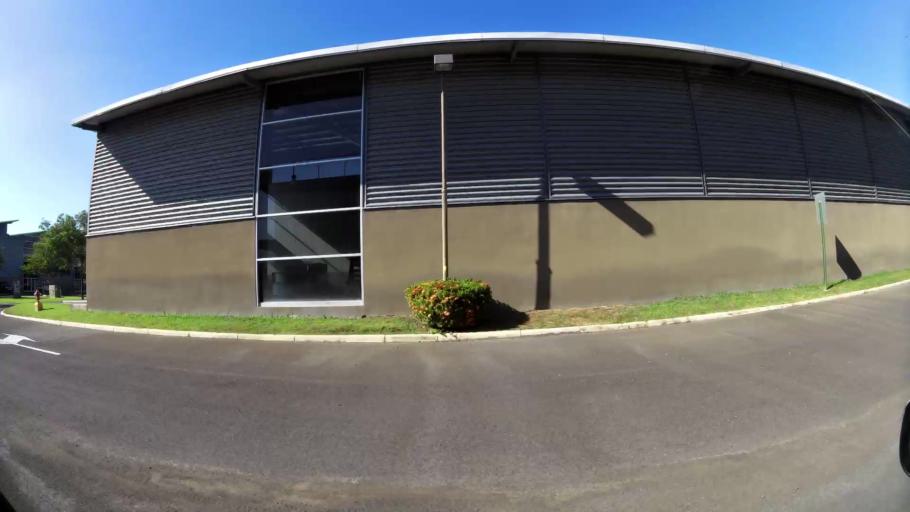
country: CR
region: Guanacaste
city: Liberia
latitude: 10.5893
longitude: -85.5338
